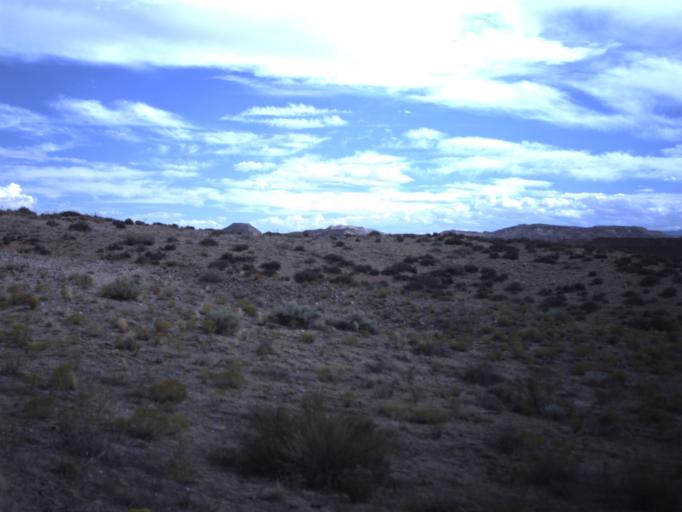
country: US
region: Utah
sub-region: San Juan County
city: Blanding
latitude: 37.2388
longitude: -109.2375
